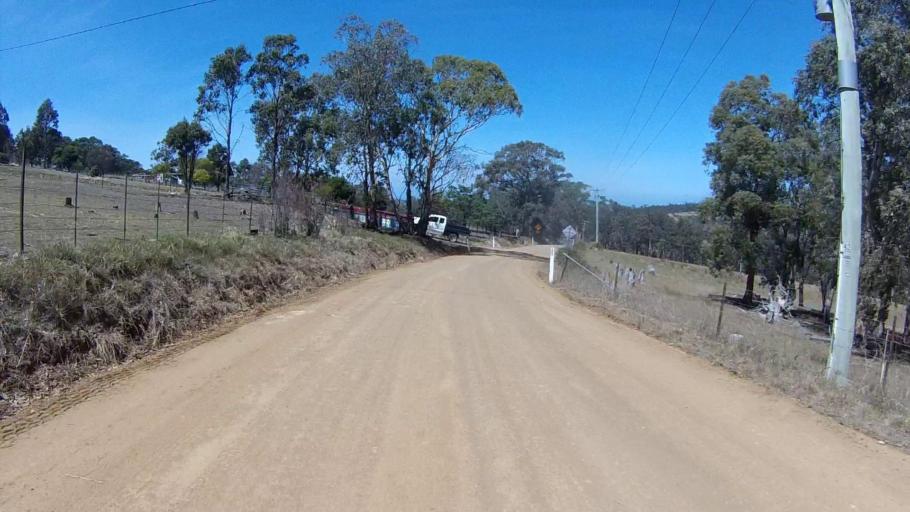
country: AU
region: Tasmania
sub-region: Sorell
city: Sorell
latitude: -42.7818
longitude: 147.6444
